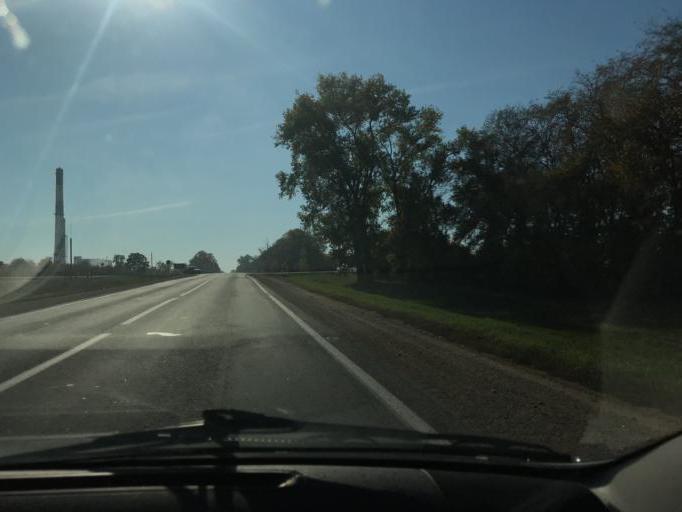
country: BY
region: Minsk
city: Starobin
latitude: 52.8014
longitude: 27.4647
